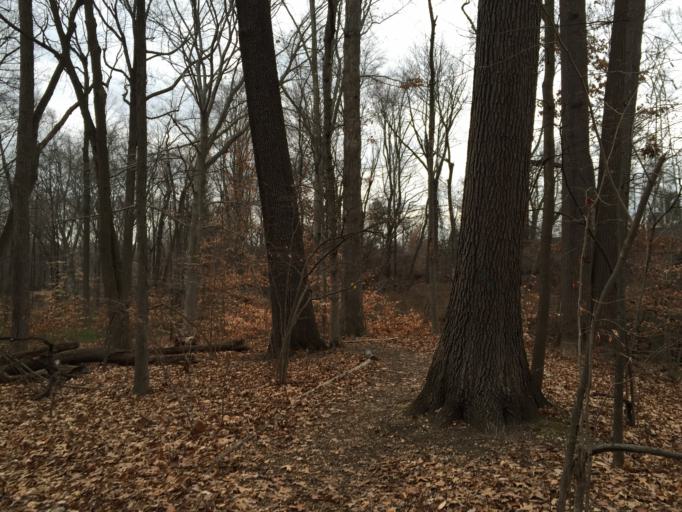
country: US
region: New Jersey
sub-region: Union County
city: New Providence
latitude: 40.7168
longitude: -74.3862
